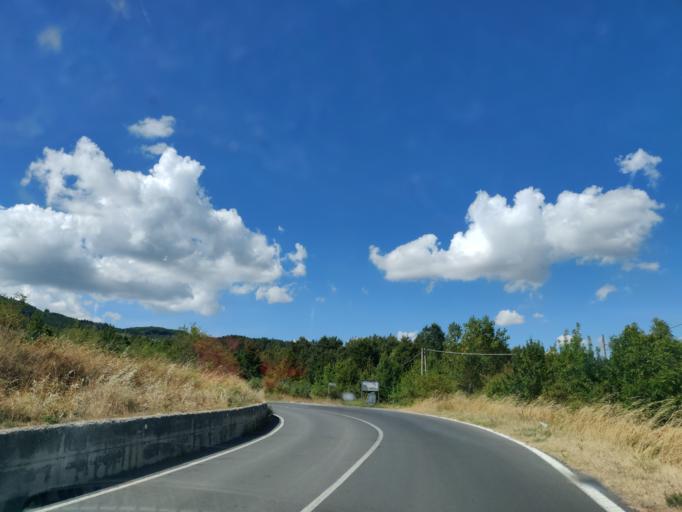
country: IT
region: Tuscany
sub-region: Provincia di Siena
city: Abbadia San Salvatore
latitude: 42.8979
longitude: 11.6687
